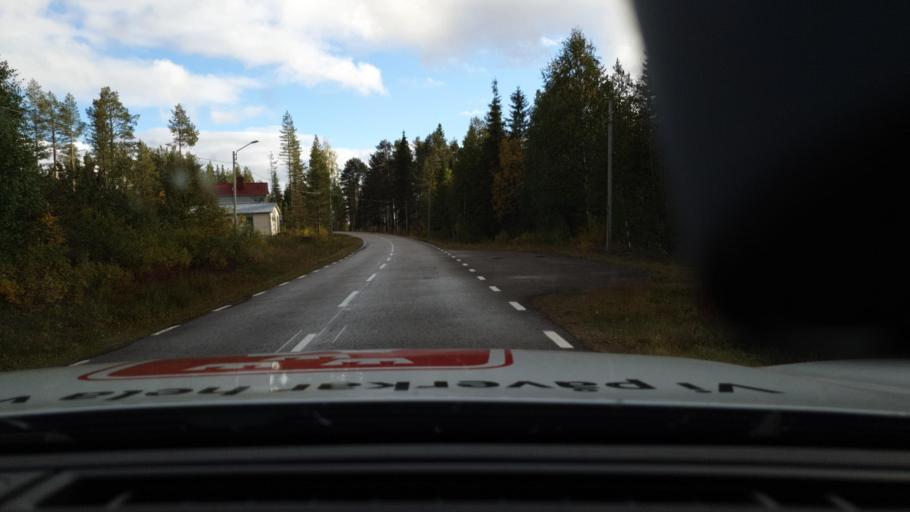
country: SE
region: Norrbotten
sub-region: Overkalix Kommun
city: OEverkalix
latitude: 67.0111
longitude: 22.4829
